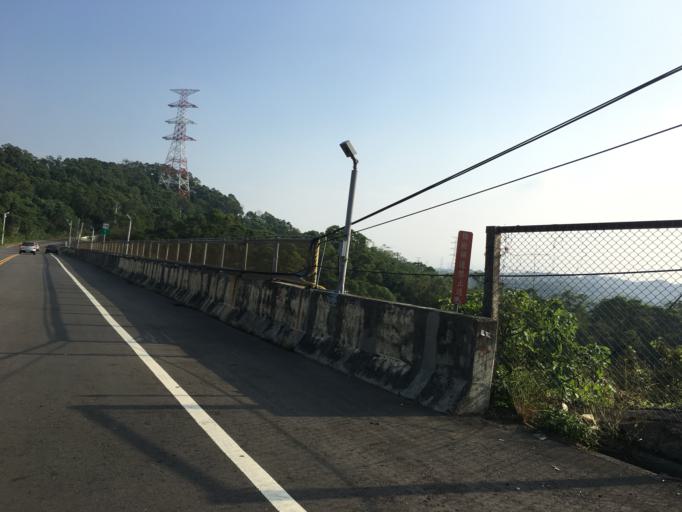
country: TW
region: Taiwan
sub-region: Hsinchu
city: Hsinchu
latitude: 24.7572
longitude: 121.0277
